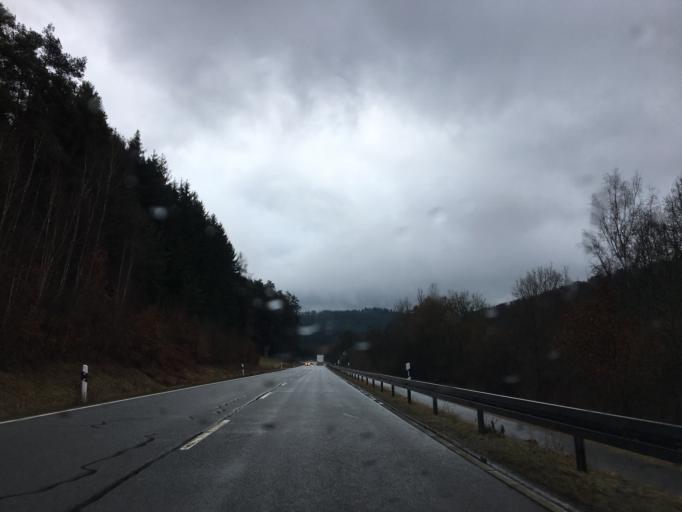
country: DE
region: Hesse
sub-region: Regierungsbezirk Darmstadt
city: Beerfelden
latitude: 49.6143
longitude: 8.9595
